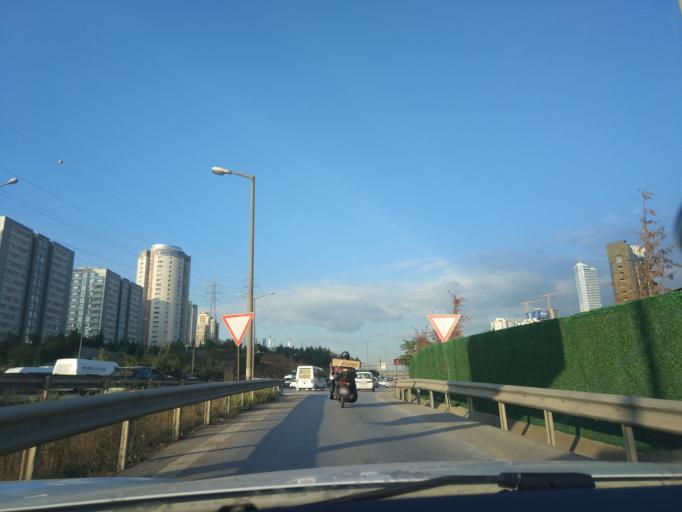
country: TR
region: Istanbul
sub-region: Atasehir
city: Atasehir
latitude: 40.9871
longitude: 29.1081
